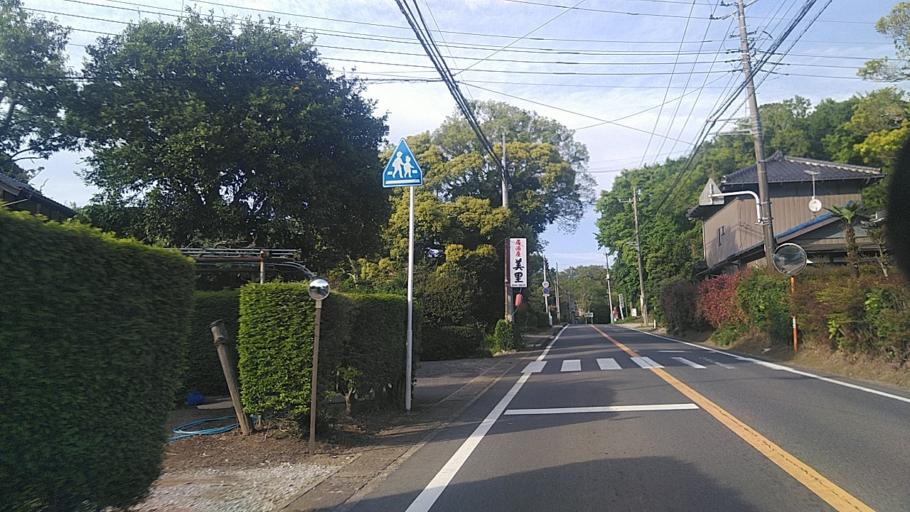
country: JP
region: Chiba
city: Shiroi
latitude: 35.7819
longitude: 140.1255
